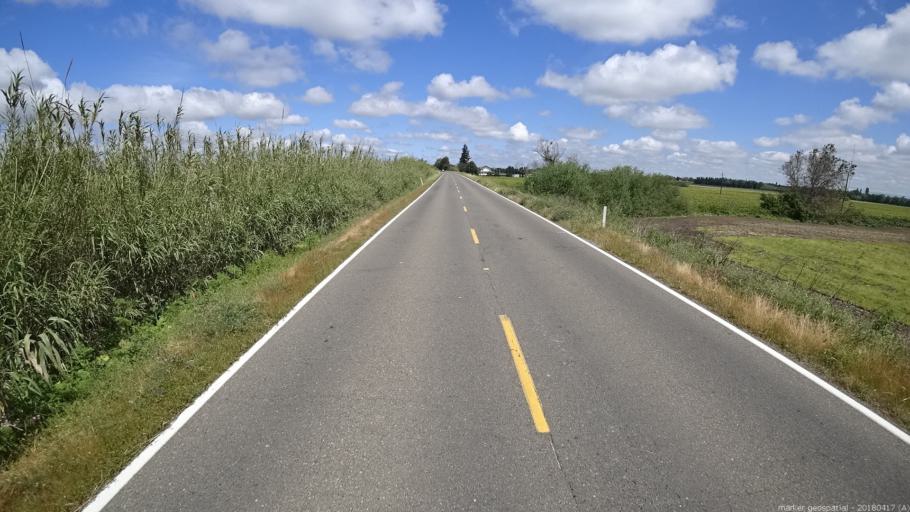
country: US
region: California
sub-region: Sacramento County
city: Walnut Grove
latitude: 38.2102
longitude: -121.5568
